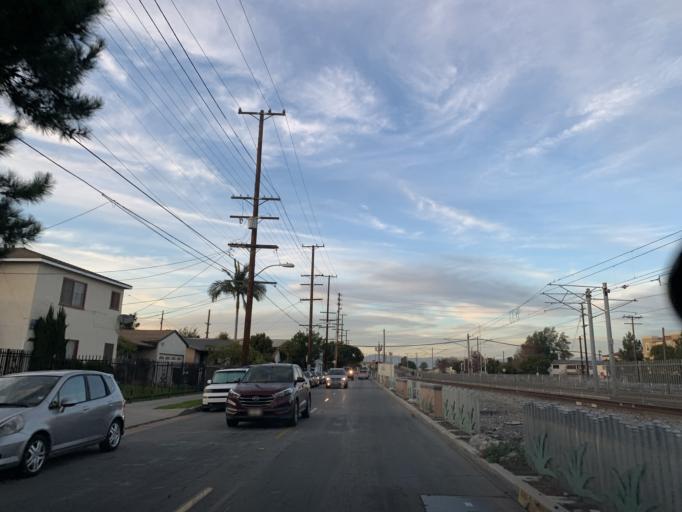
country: US
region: California
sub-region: Los Angeles County
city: Compton
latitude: 33.8995
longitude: -118.2246
